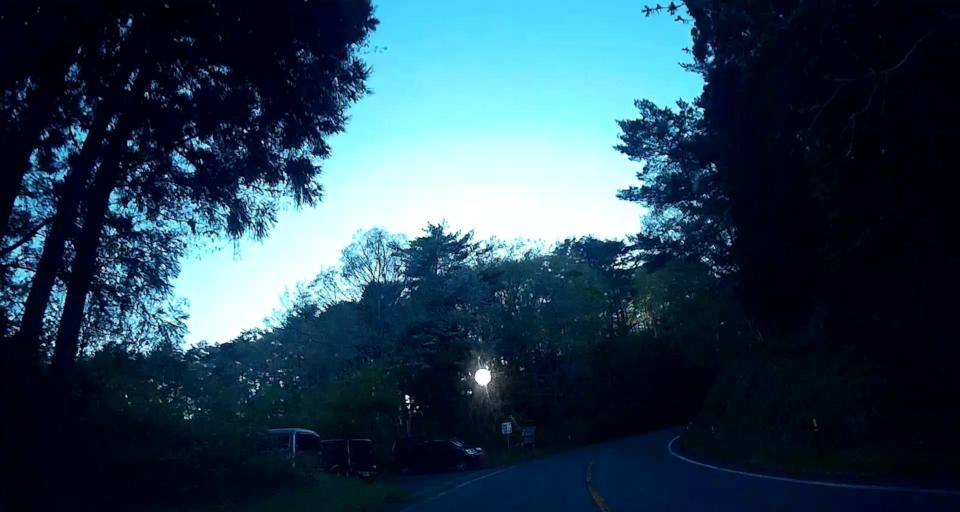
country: JP
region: Iwate
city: Miyako
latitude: 39.6526
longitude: 141.9676
